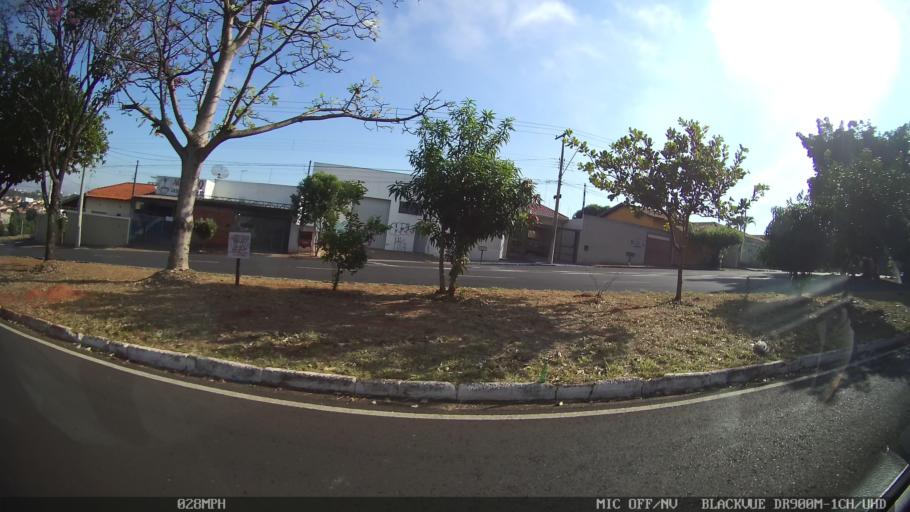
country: BR
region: Sao Paulo
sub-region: Sao Jose Do Rio Preto
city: Sao Jose do Rio Preto
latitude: -20.7934
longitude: -49.4217
